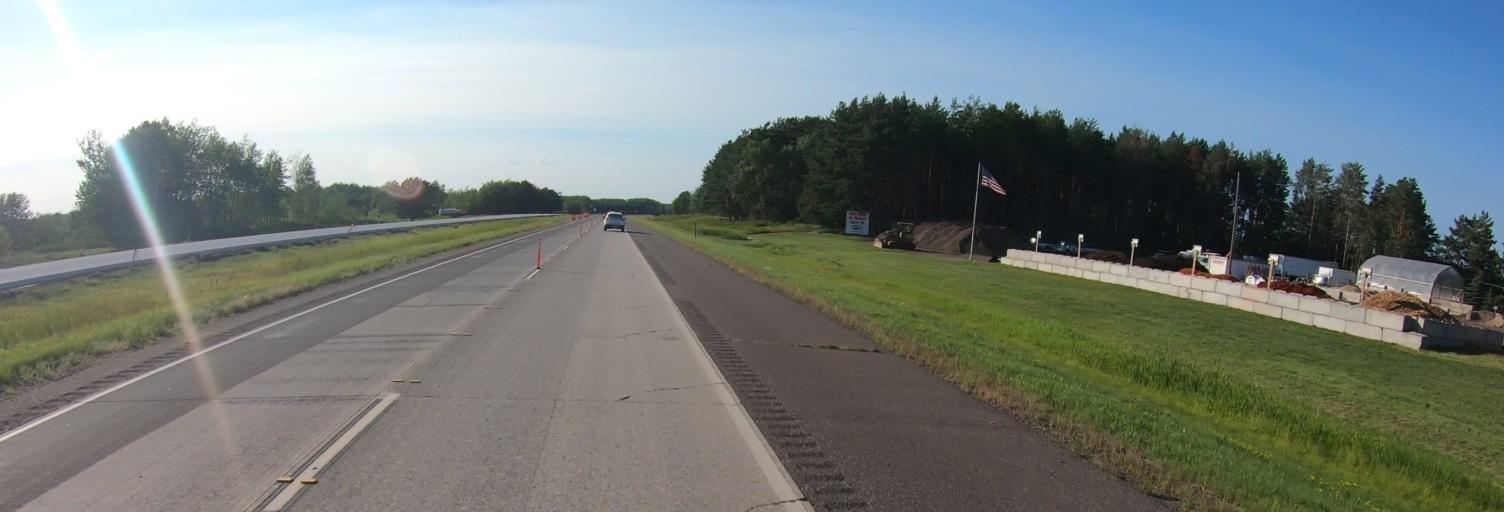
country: US
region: Minnesota
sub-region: Saint Louis County
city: Hermantown
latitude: 46.8672
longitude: -92.3309
